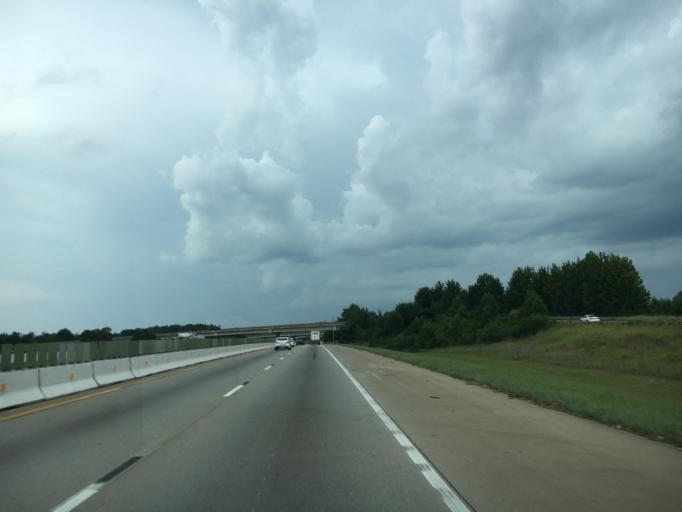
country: US
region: South Carolina
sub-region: Spartanburg County
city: Southern Shops
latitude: 34.9792
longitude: -82.0078
